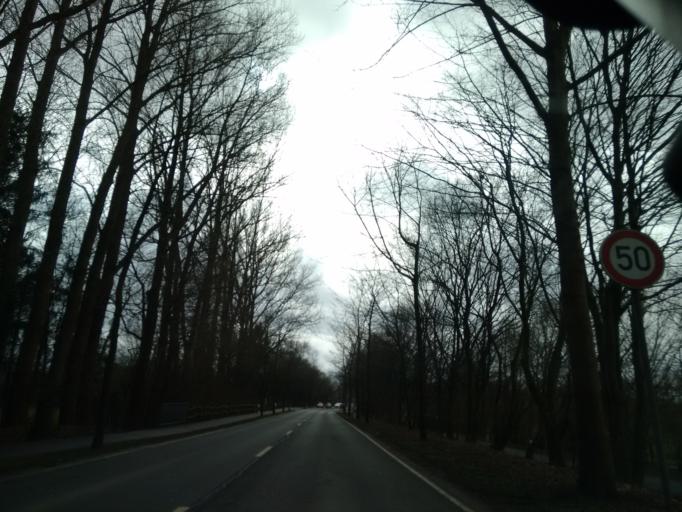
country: DE
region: North Rhine-Westphalia
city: Bad Lippspringe
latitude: 51.7692
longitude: 8.7976
